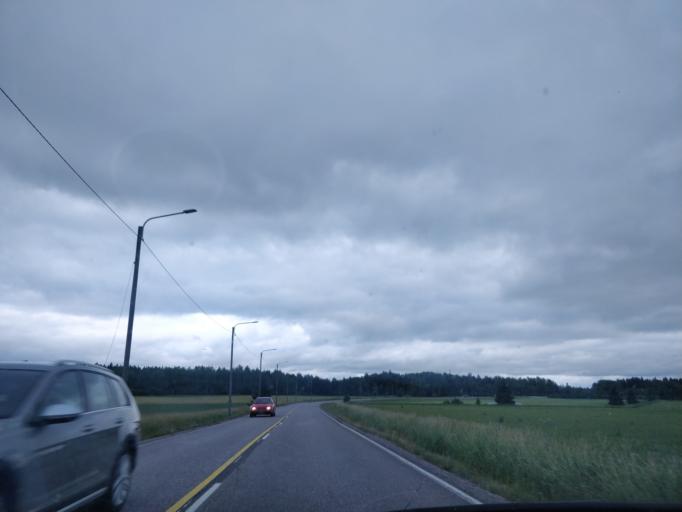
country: FI
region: Uusimaa
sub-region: Helsinki
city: Kauniainen
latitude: 60.2897
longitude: 24.7000
